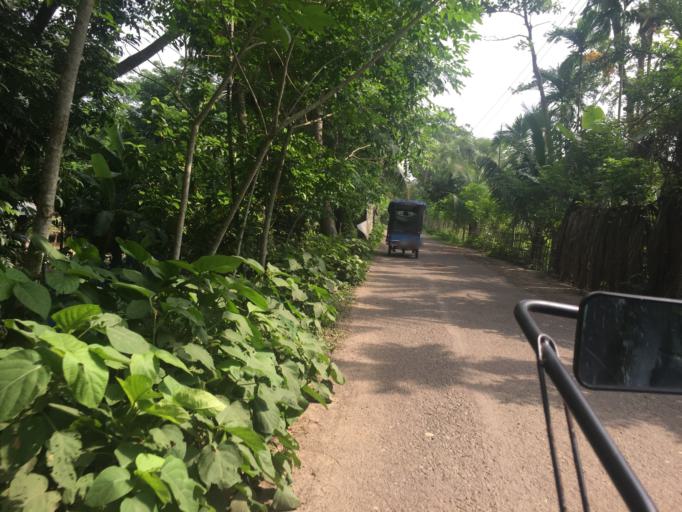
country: BD
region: Barisal
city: Mathba
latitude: 22.2195
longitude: 89.9159
